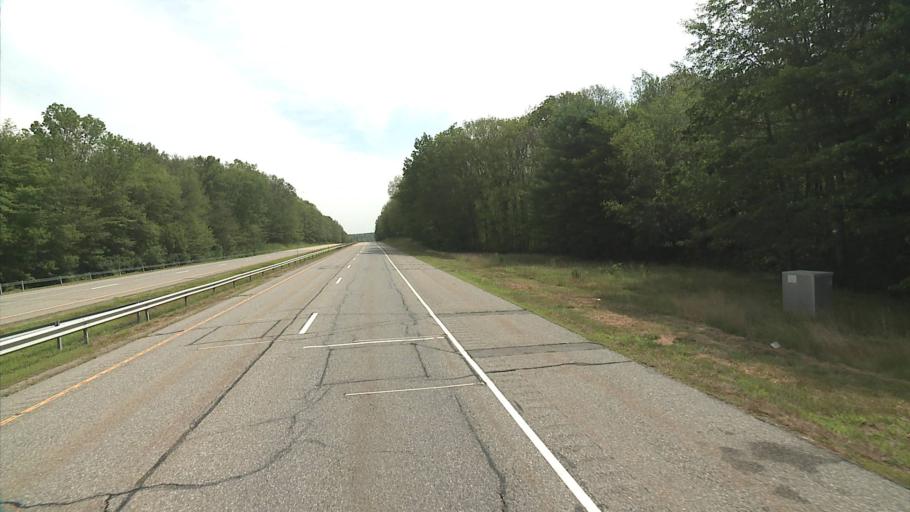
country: US
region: Connecticut
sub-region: Windham County
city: Danielson
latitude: 41.7718
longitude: -71.8573
